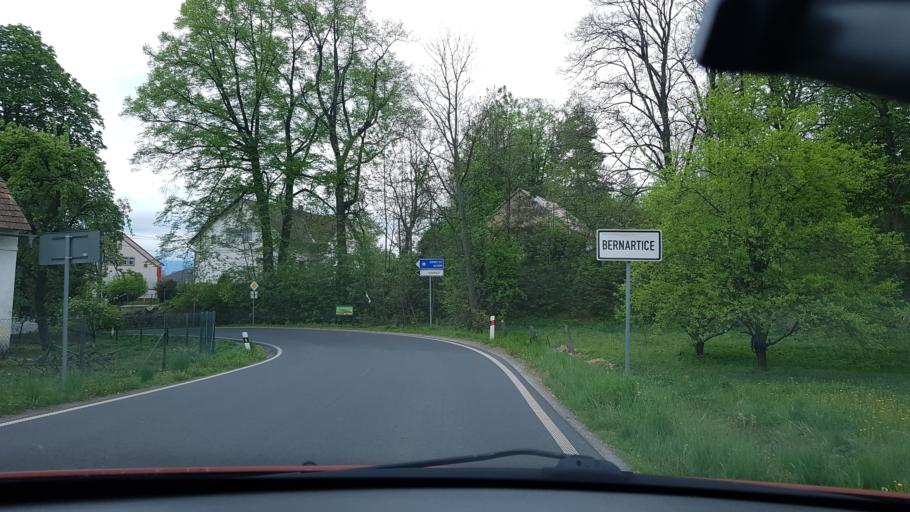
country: CZ
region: Olomoucky
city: Javornik
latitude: 50.3907
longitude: 17.0771
